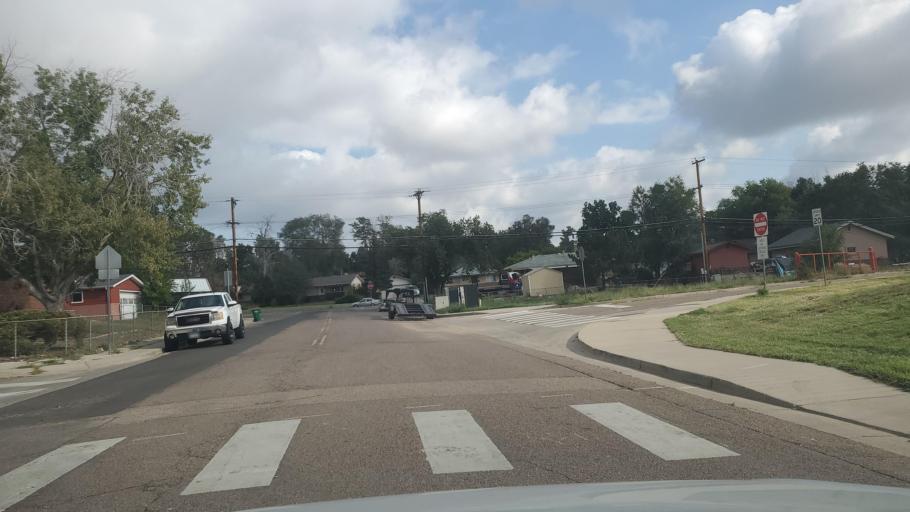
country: US
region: Colorado
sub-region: Adams County
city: Welby
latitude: 39.8484
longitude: -104.9709
